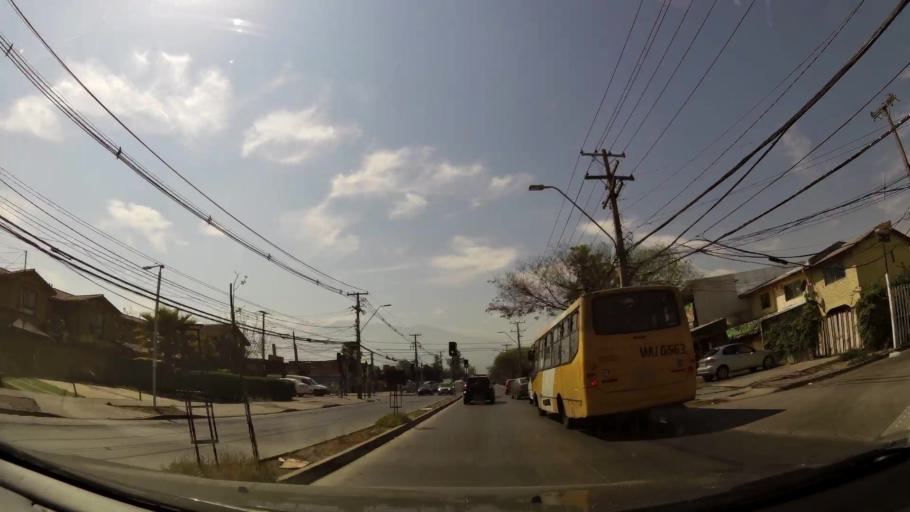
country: CL
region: Santiago Metropolitan
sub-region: Provincia de Cordillera
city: Puente Alto
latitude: -33.5808
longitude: -70.5929
